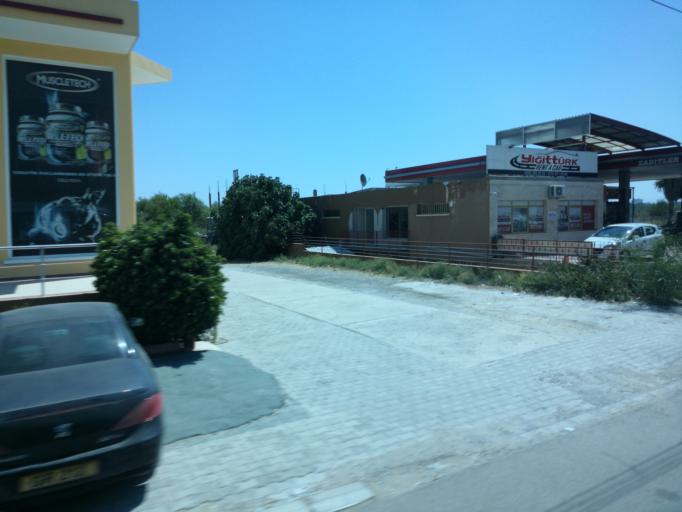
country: CY
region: Ammochostos
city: Famagusta
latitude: 35.1469
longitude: 33.9104
